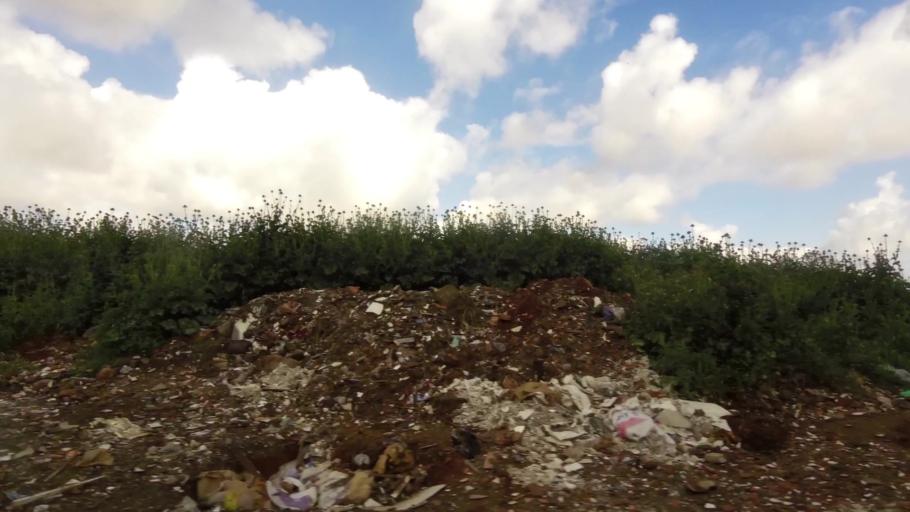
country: MA
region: Grand Casablanca
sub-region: Nouaceur
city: Bouskoura
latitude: 33.5359
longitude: -7.6980
